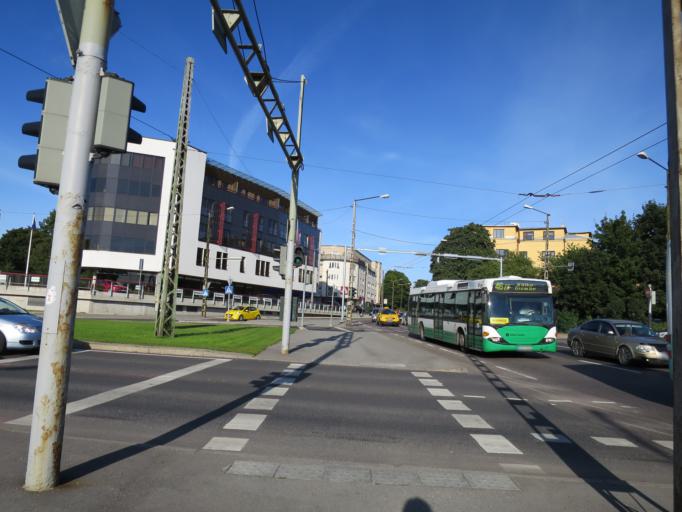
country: EE
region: Harju
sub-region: Tallinna linn
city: Tallinn
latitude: 59.4287
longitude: 24.7258
